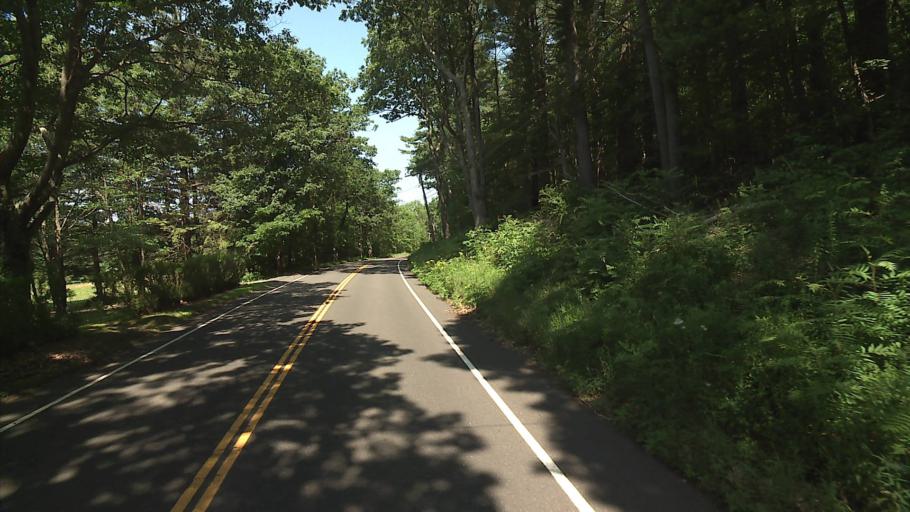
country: US
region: Massachusetts
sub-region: Berkshire County
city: New Marlborough
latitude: 42.0233
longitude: -73.2048
